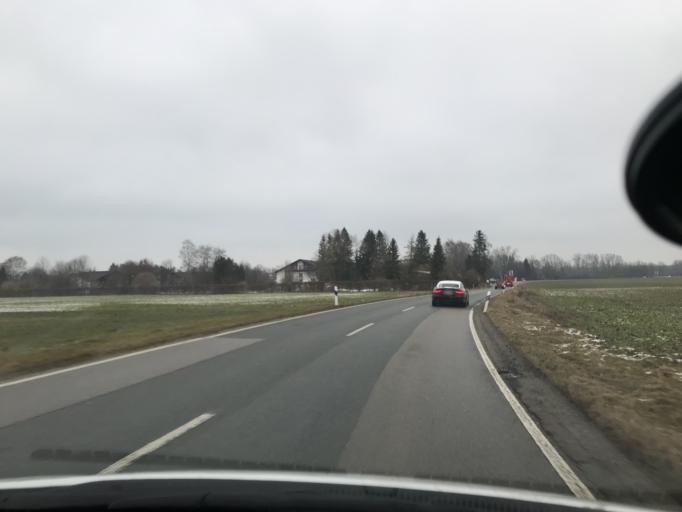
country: DE
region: Bavaria
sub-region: Upper Bavaria
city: Bad Feilnbach
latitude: 47.7858
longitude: 12.0102
